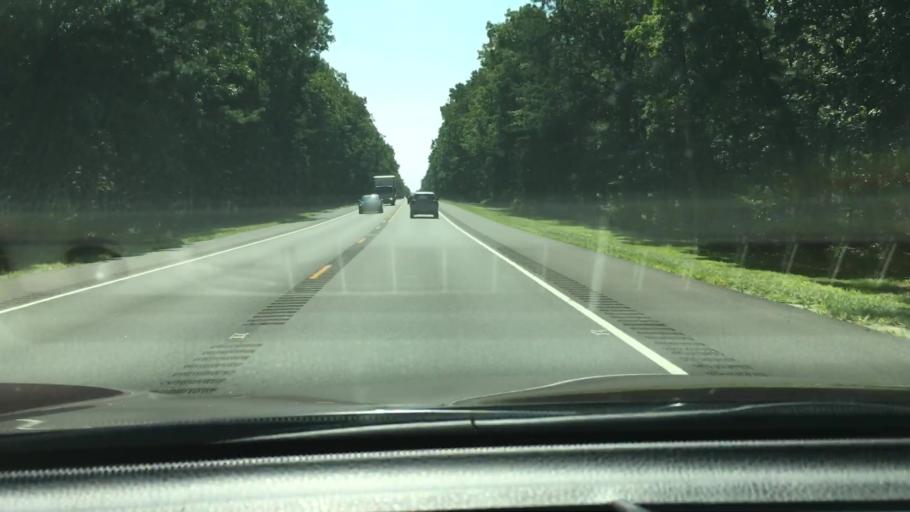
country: US
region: New Jersey
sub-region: Cumberland County
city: Laurel Lake
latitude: 39.3448
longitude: -74.8996
